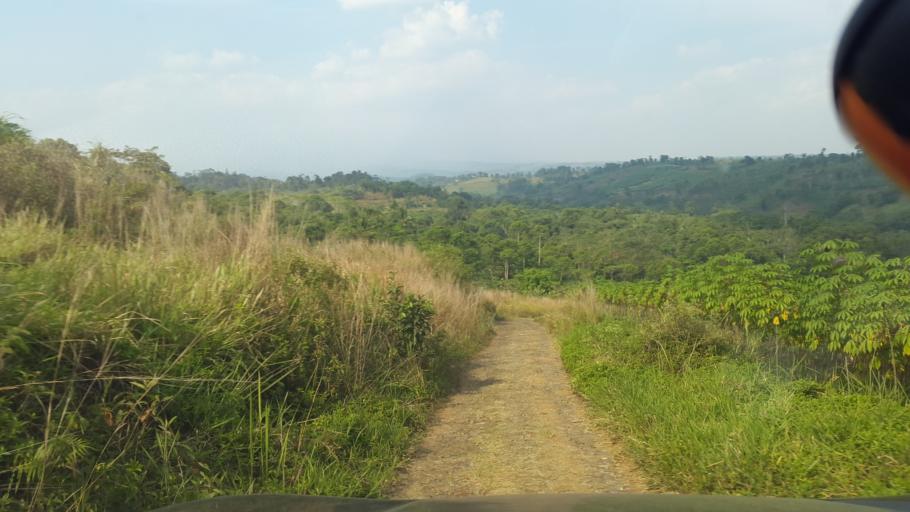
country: ID
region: West Java
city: Cicurug
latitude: -6.8324
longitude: 106.7828
